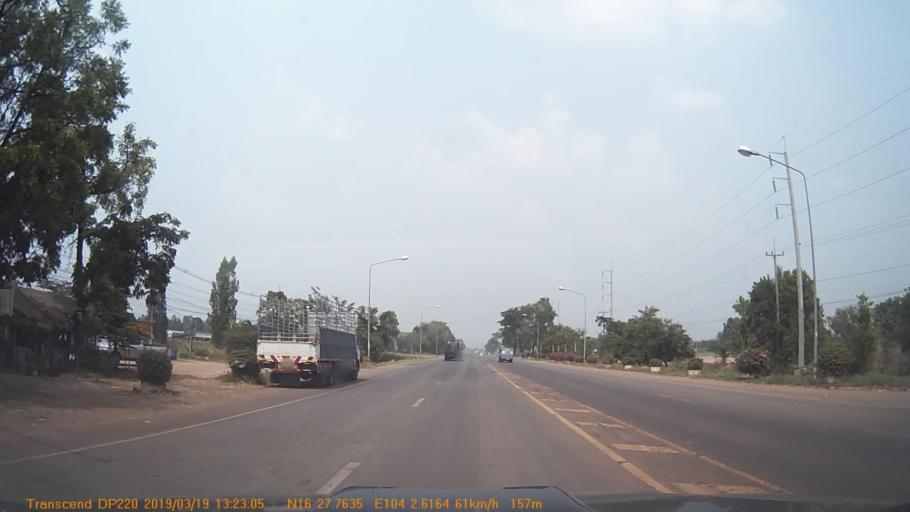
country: TH
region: Kalasin
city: Kuchinarai
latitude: 16.4630
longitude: 104.0437
